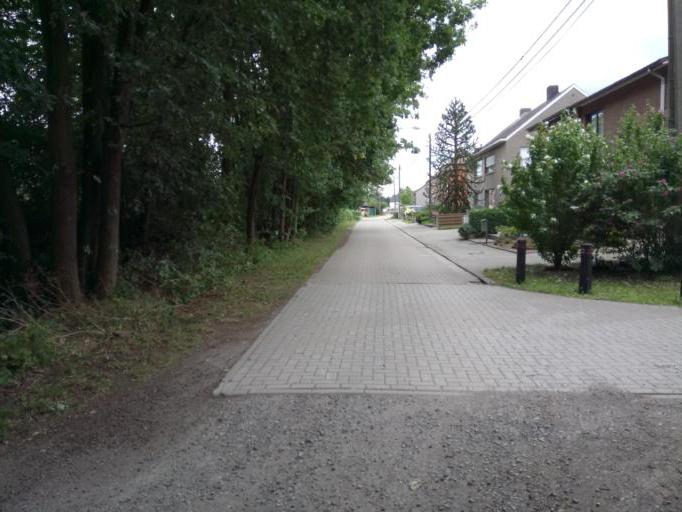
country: BE
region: Flanders
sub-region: Provincie Antwerpen
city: Mol
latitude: 51.2137
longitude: 5.1308
